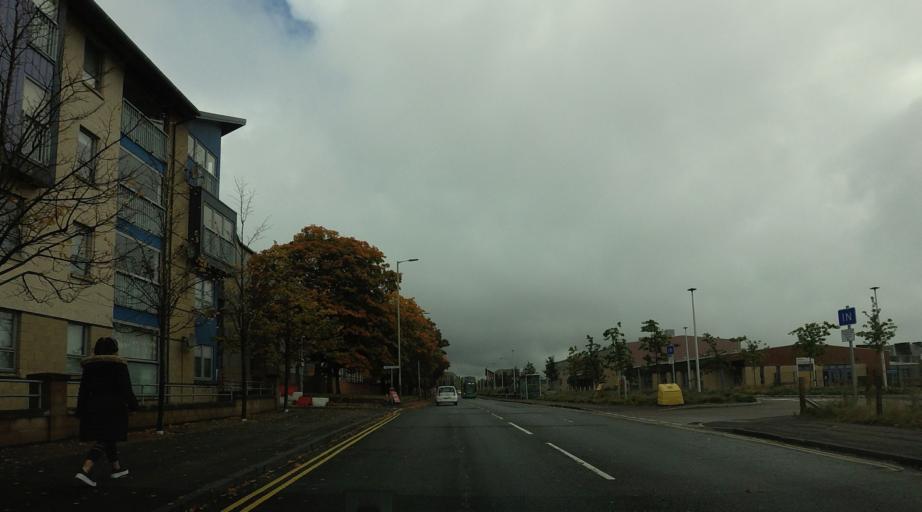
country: GB
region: Scotland
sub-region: Dundee City
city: Dundee
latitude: 56.4682
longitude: -2.9729
